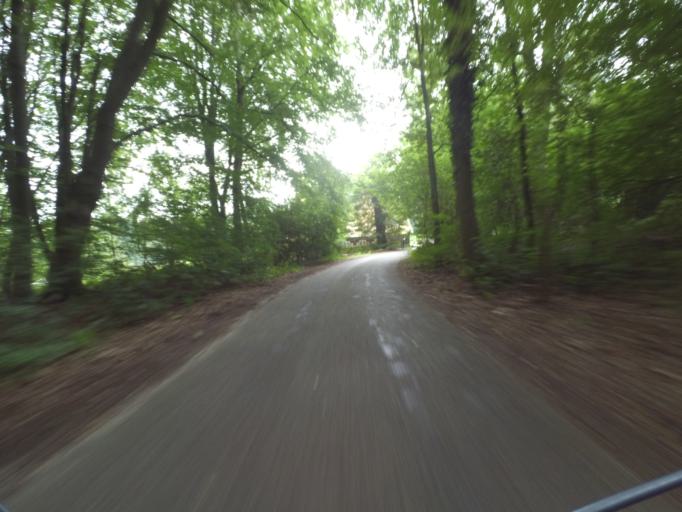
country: NL
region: Overijssel
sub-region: Gemeente Oldenzaal
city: Oldenzaal
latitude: 52.3231
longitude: 6.9572
